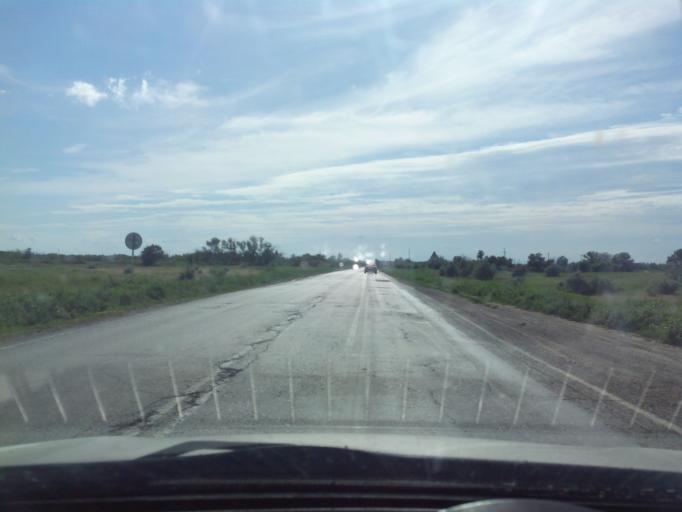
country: RU
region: Astrakhan
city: Kapustin Yar
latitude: 48.5616
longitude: 45.7724
